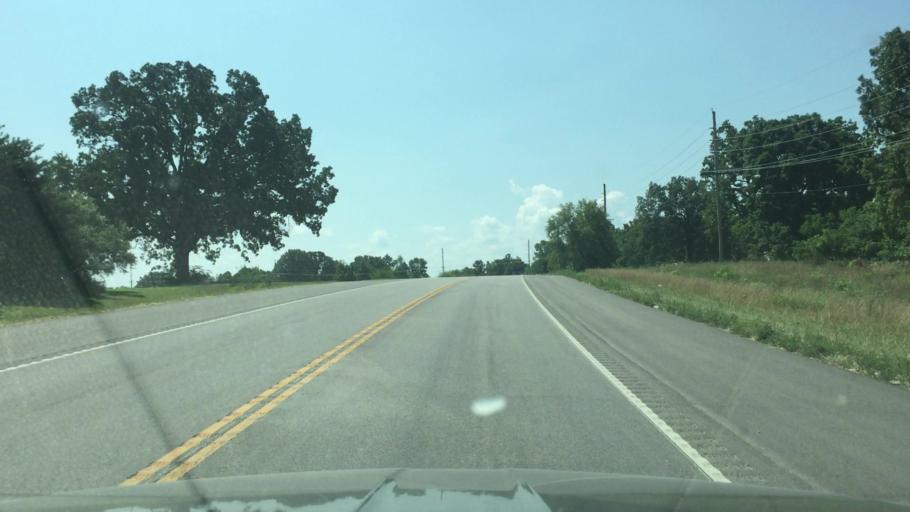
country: US
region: Missouri
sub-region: Miller County
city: Eldon
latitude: 38.3688
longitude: -92.6161
